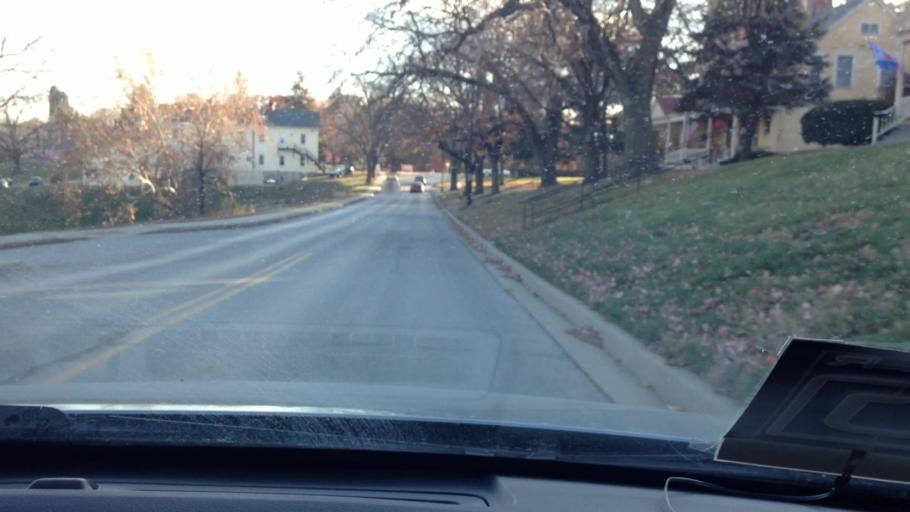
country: US
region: Kansas
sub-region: Leavenworth County
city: Leavenworth
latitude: 39.3571
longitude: -94.9165
